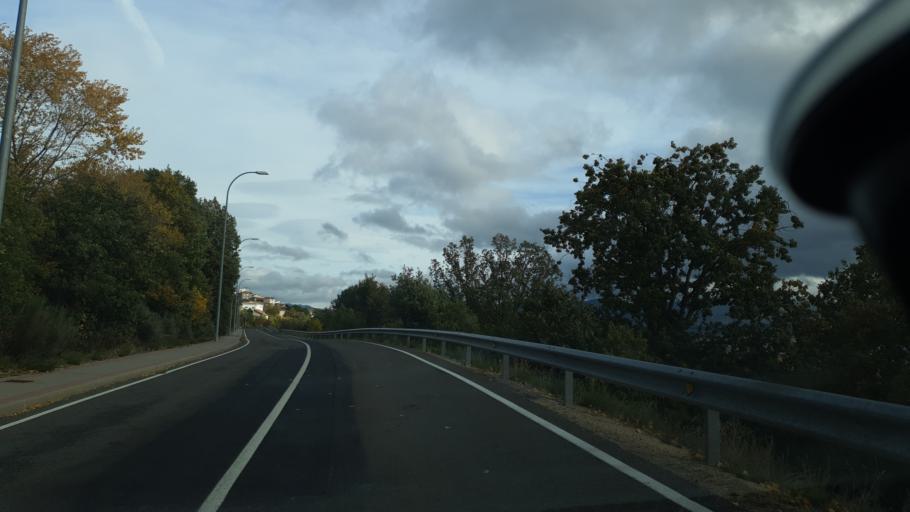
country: ES
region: Castille and Leon
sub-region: Provincia de Avila
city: Hoyocasero
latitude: 40.3997
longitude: -4.9829
